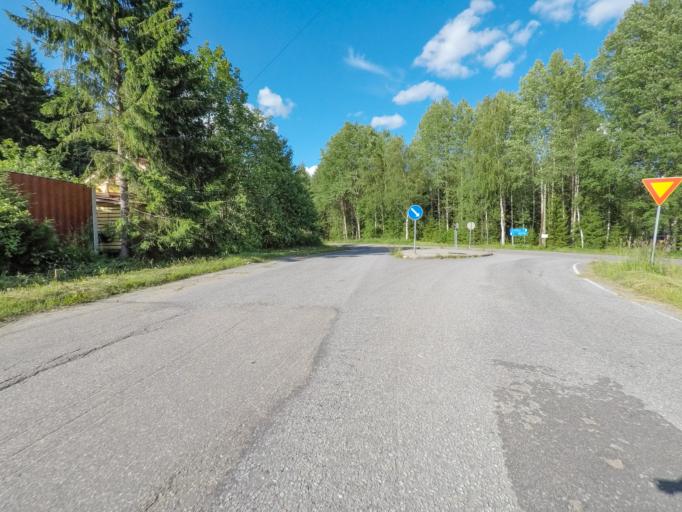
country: FI
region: South Karelia
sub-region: Imatra
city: Imatra
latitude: 61.1410
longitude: 28.7424
